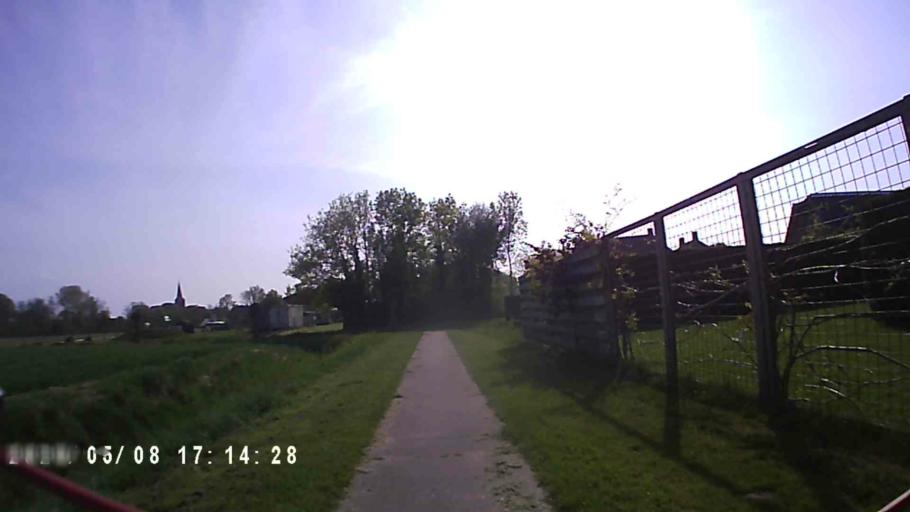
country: NL
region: Groningen
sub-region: Gemeente Winsum
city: Winsum
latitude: 53.3963
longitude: 6.5636
